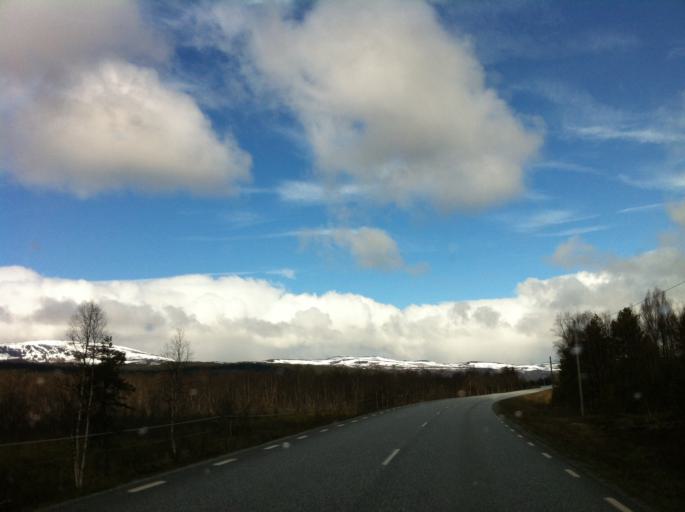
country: SE
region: Jaemtland
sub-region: Are Kommun
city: Are
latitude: 62.5891
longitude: 12.5520
